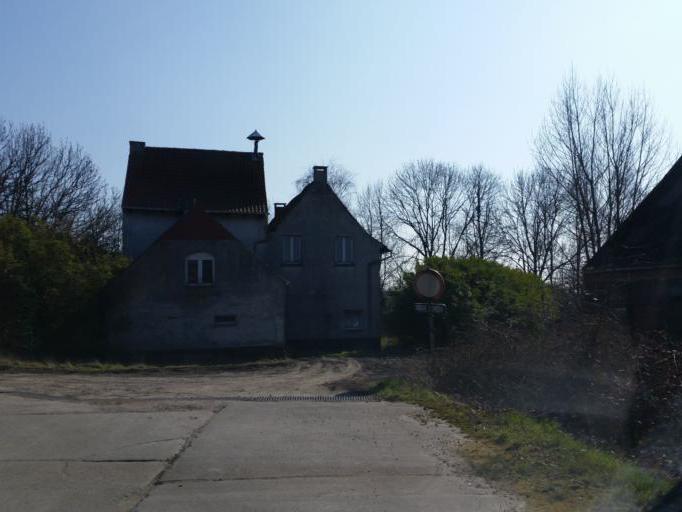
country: BE
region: Flanders
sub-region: Provincie Oost-Vlaanderen
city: Kruibeke
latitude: 51.1914
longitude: 4.3281
